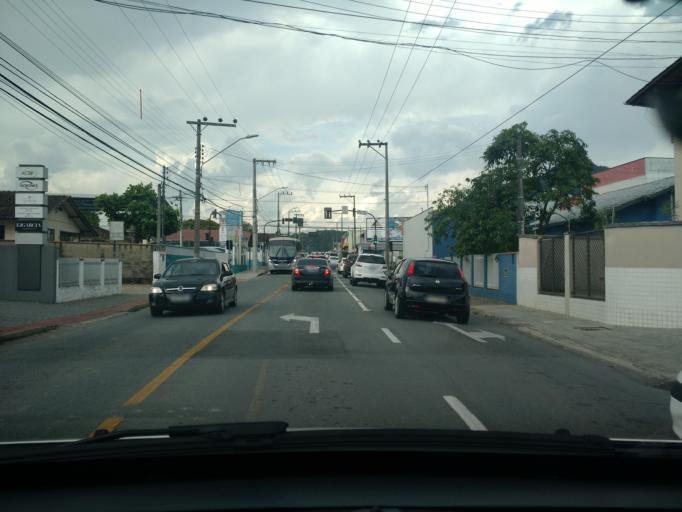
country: BR
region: Santa Catarina
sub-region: Jaragua Do Sul
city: Jaragua do Sul
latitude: -26.4842
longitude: -49.0925
